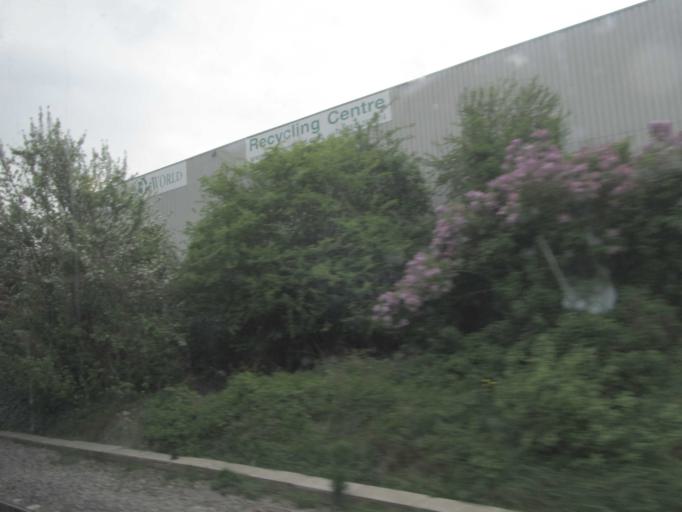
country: GB
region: England
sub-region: Slough
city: Slough
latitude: 51.5169
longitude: -0.6142
